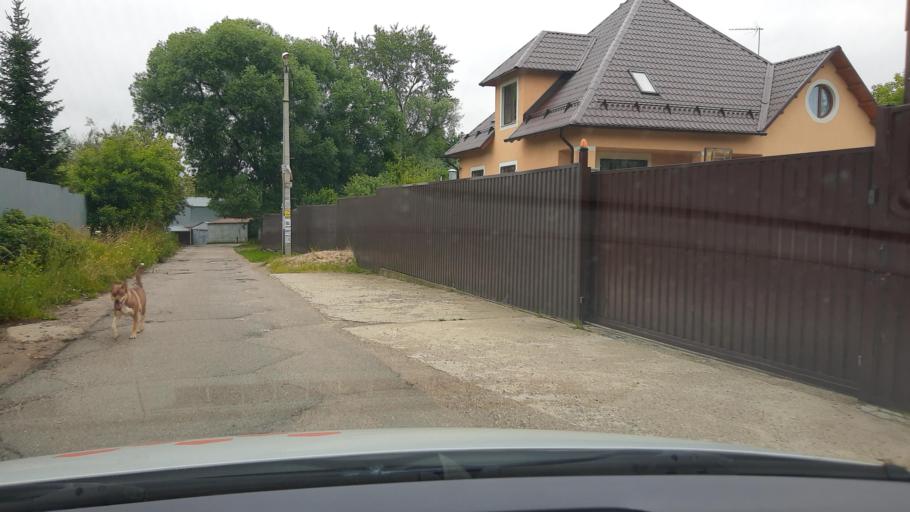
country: RU
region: Moskovskaya
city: Gorki-Leninskiye
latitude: 55.4976
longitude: 37.8252
